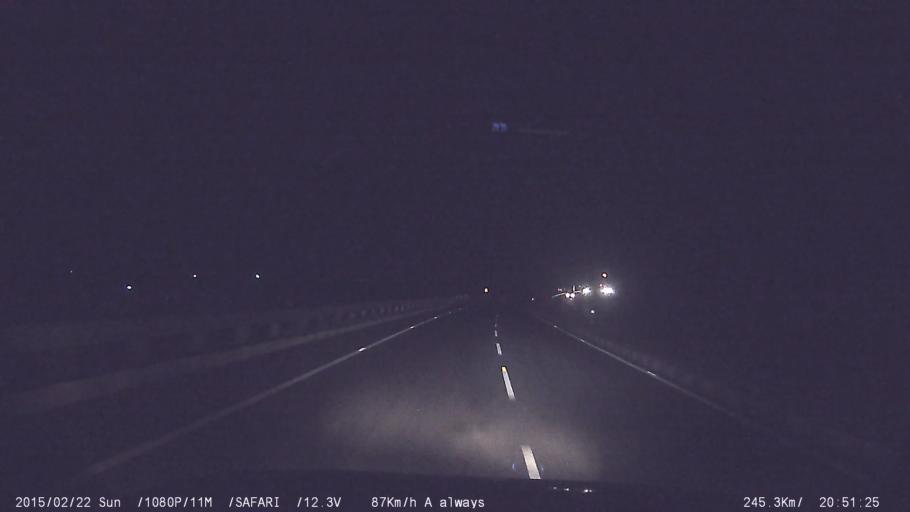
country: IN
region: Tamil Nadu
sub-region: Dindigul
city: Vedasandur
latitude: 10.5440
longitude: 77.9402
